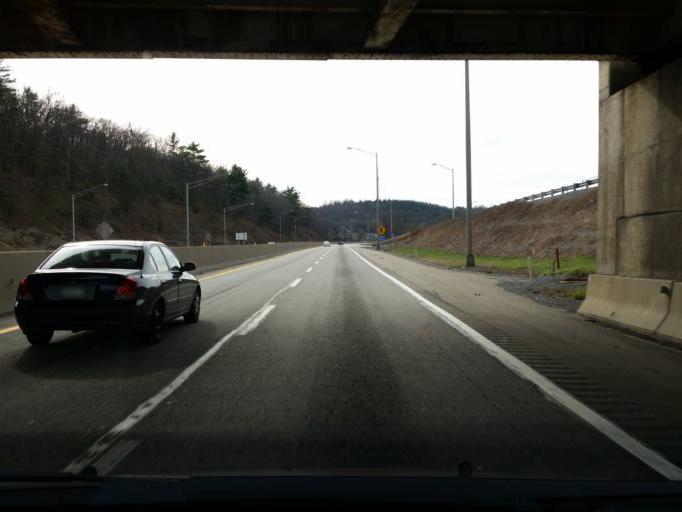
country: US
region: Pennsylvania
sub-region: Fulton County
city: McConnellsburg
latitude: 40.0518
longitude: -77.9592
